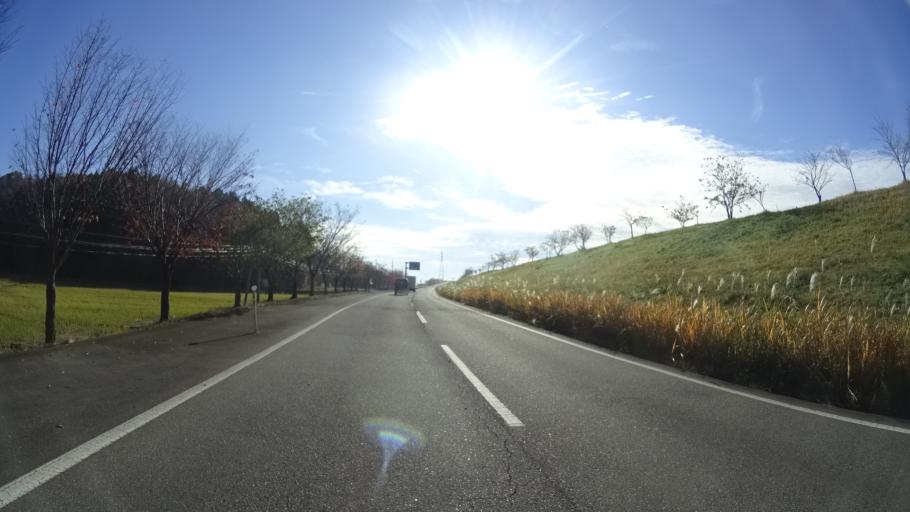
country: JP
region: Niigata
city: Yoshida-kasugacho
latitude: 37.6487
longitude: 138.8161
